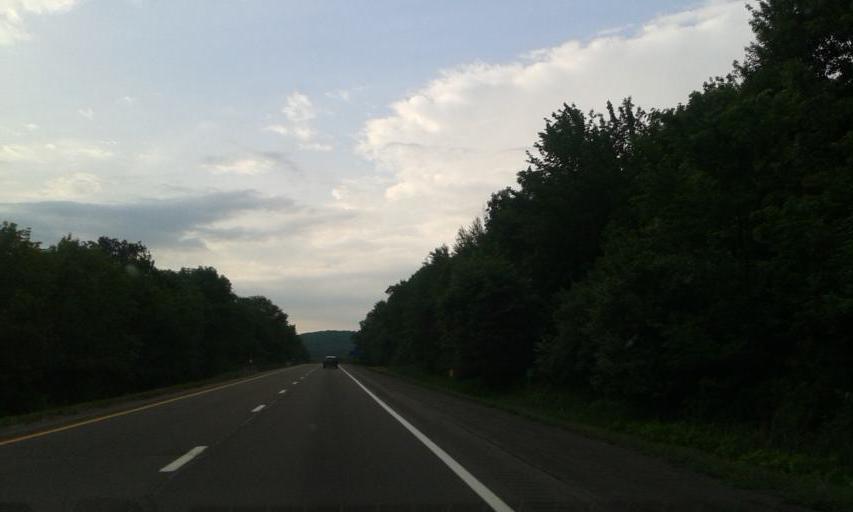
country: US
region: Pennsylvania
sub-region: Susquehanna County
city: Hallstead
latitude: 42.0289
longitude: -75.7861
